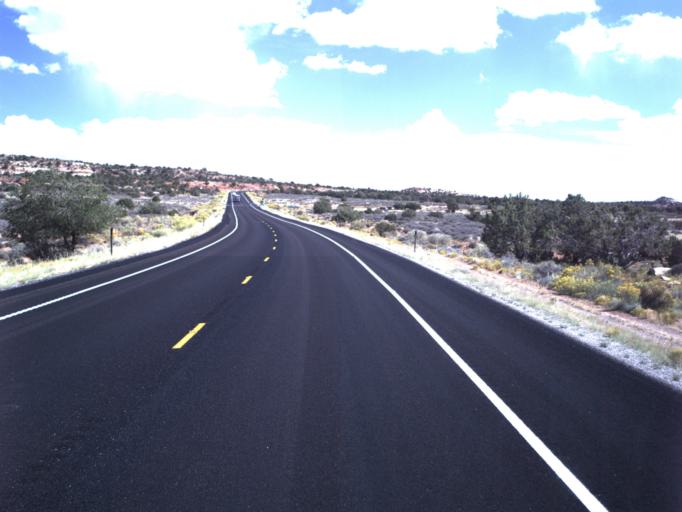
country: US
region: Utah
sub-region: Grand County
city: Moab
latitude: 38.5857
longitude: -109.8045
